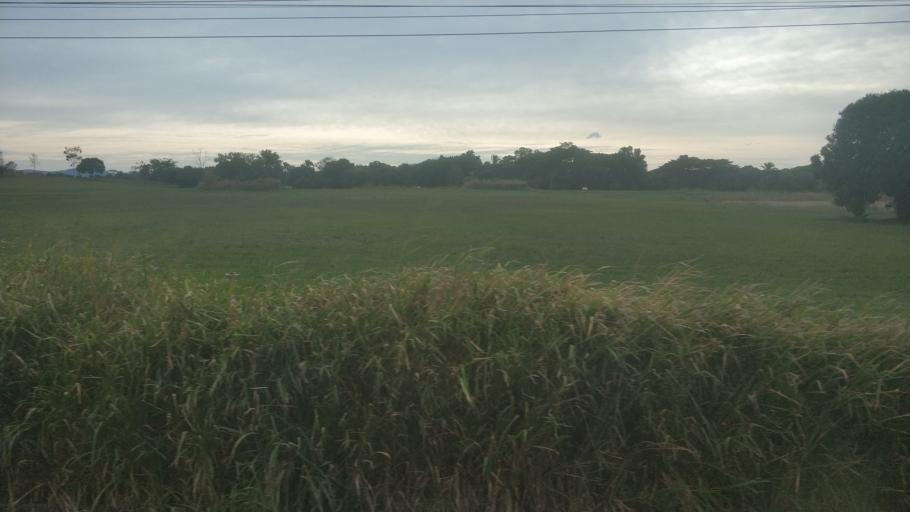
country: BR
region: Rio de Janeiro
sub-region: Seropedica
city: Seropedica
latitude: -22.7625
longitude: -43.6849
